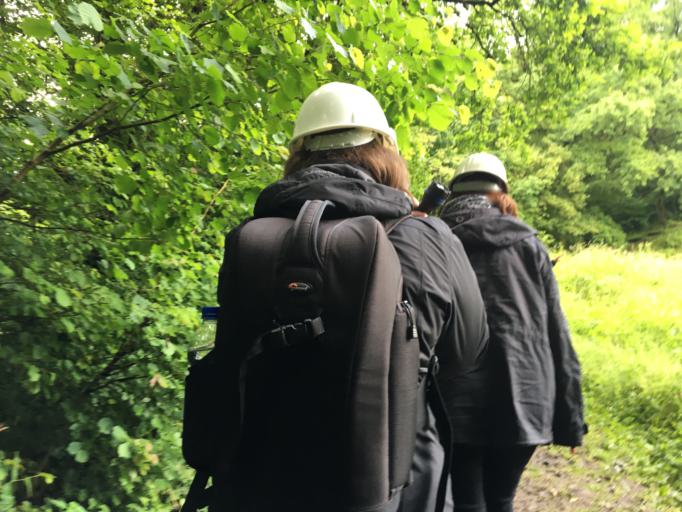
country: FR
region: Lorraine
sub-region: Departement de la Meuse
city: Clermont-en-Argonne
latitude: 49.2047
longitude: 5.0678
